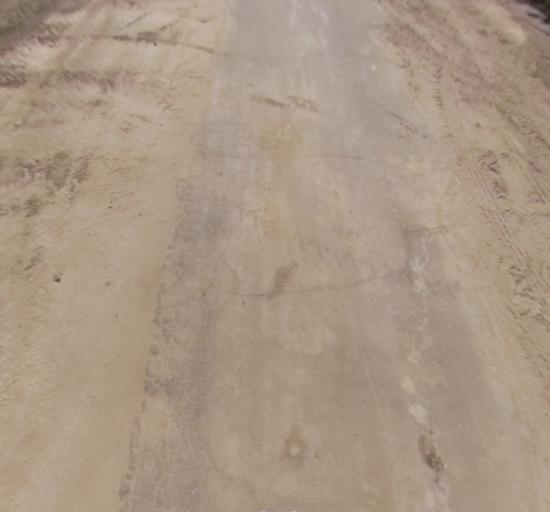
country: US
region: California
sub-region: Madera County
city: Chowchilla
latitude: 37.0254
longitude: -120.4032
